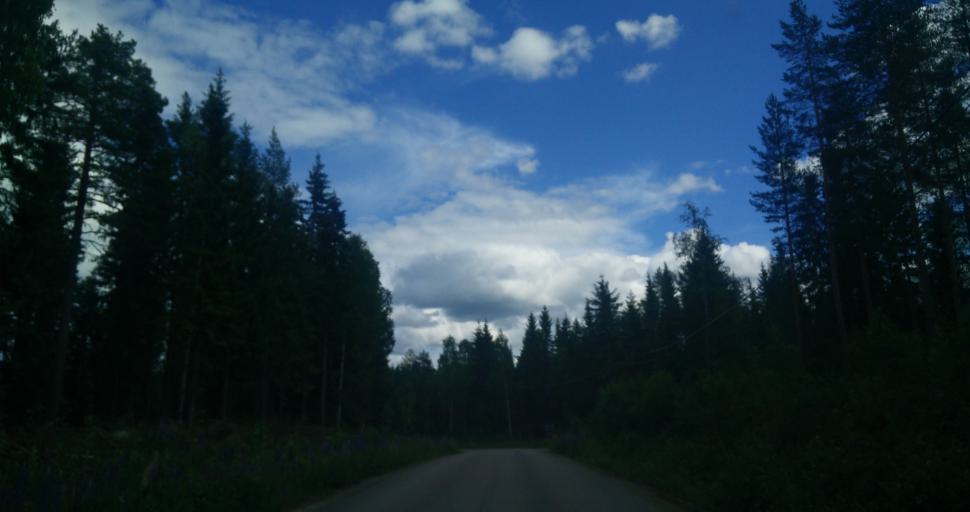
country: SE
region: Gaevleborg
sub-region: Nordanstigs Kommun
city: Bergsjoe
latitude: 62.0550
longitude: 16.8299
